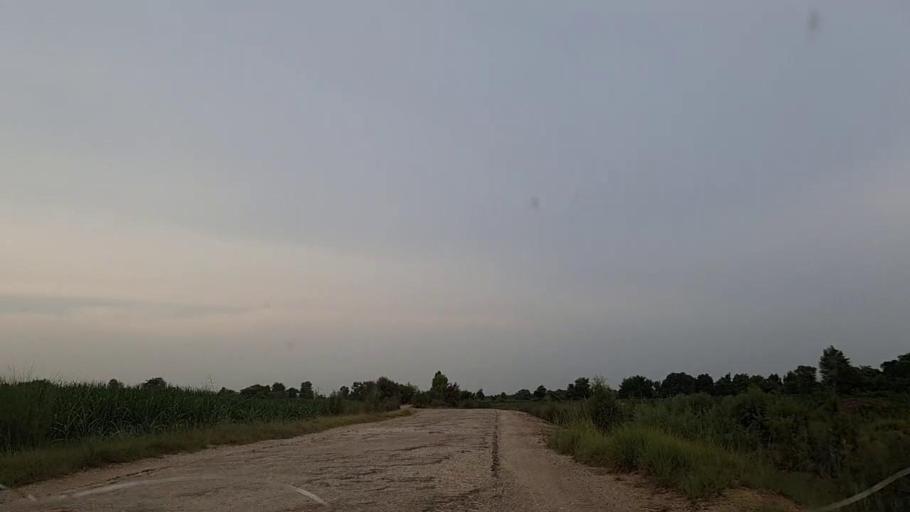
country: PK
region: Sindh
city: Mirpur Mathelo
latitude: 27.8845
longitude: 69.6390
